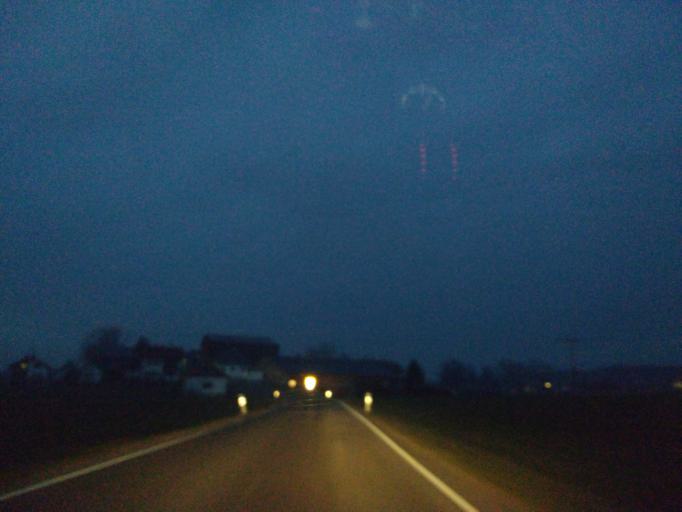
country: DE
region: Bavaria
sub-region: Swabia
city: Stottwang
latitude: 47.8780
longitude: 10.6985
